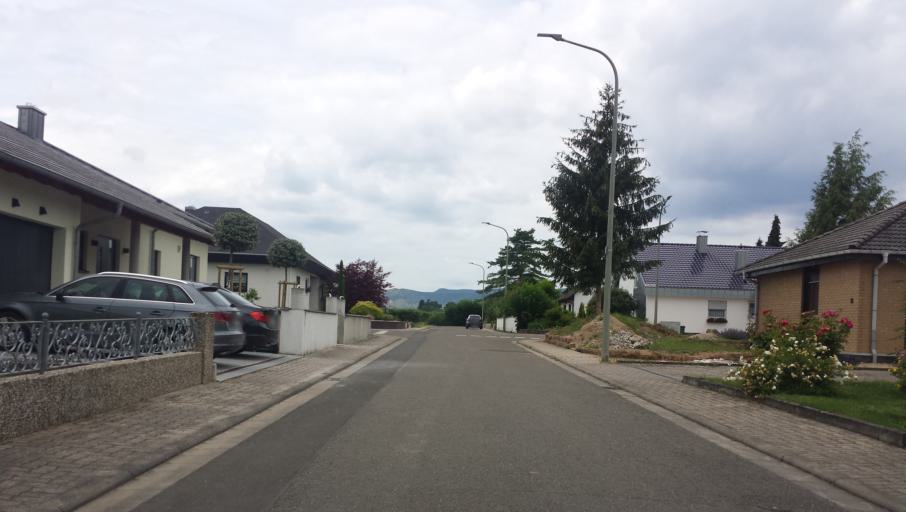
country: DE
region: Rheinland-Pfalz
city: Knoringen
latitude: 49.2347
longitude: 8.1410
